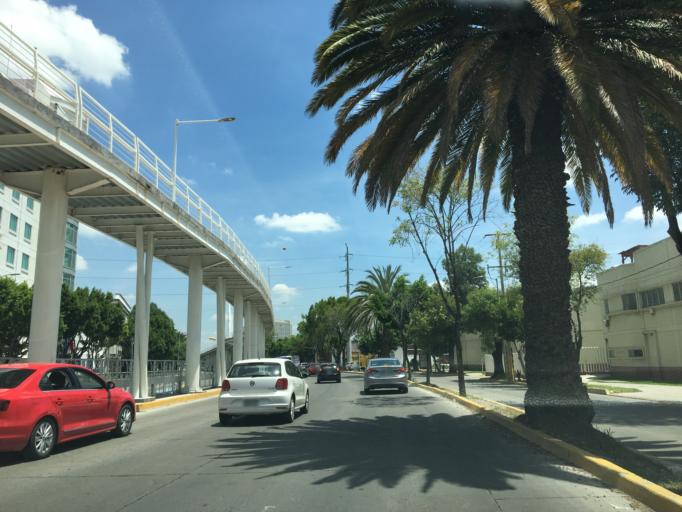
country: MX
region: Puebla
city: Puebla
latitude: 19.0591
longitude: -98.2195
